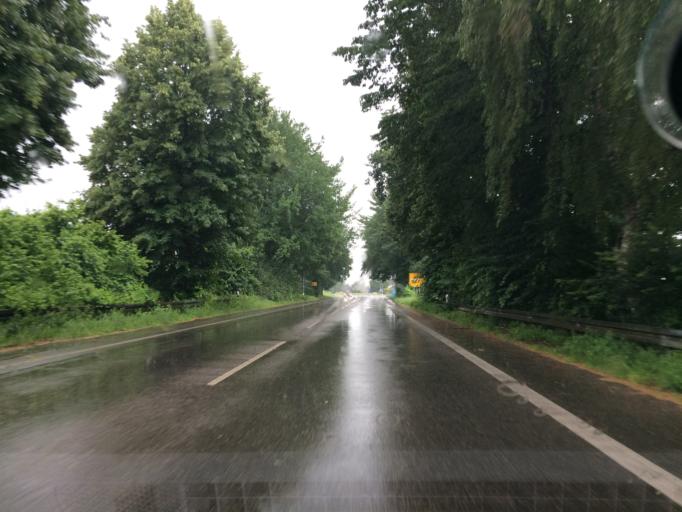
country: DE
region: North Rhine-Westphalia
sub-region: Regierungsbezirk Munster
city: Haltern
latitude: 51.7541
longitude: 7.1937
